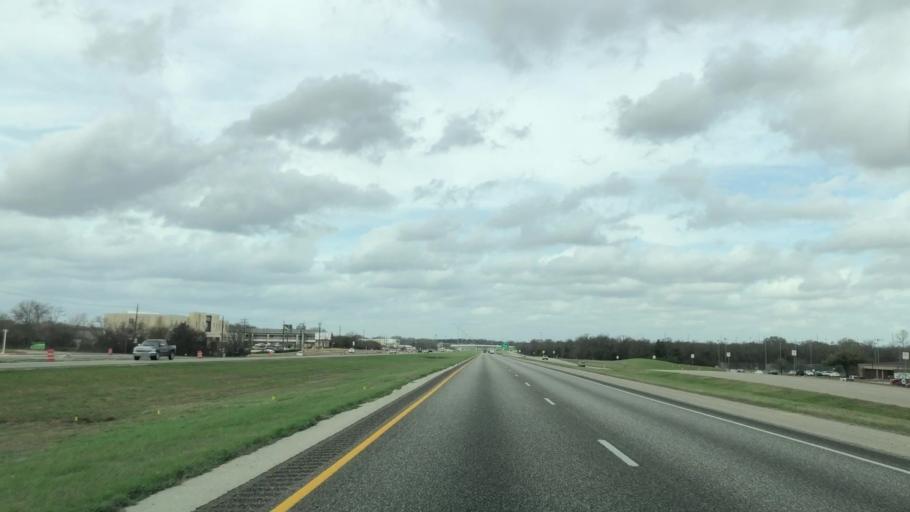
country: US
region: Texas
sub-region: Brazos County
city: Bryan
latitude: 30.6774
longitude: -96.3419
